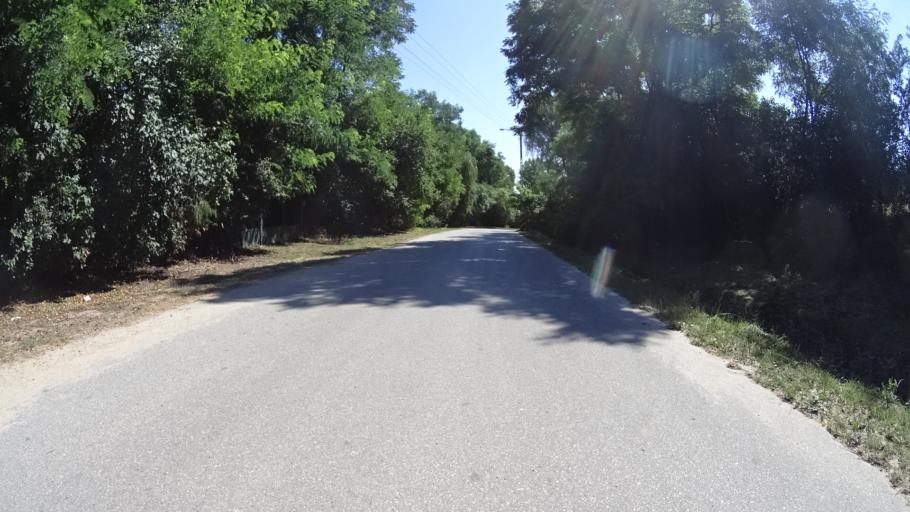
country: PL
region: Masovian Voivodeship
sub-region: Powiat bialobrzeski
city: Bialobrzegi
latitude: 51.6672
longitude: 20.9173
